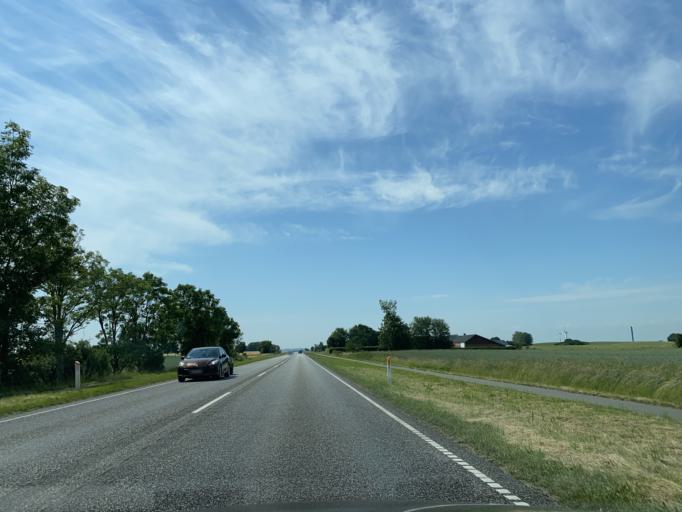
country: DK
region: South Denmark
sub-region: Haderslev Kommune
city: Haderslev
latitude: 55.2114
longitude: 9.4800
